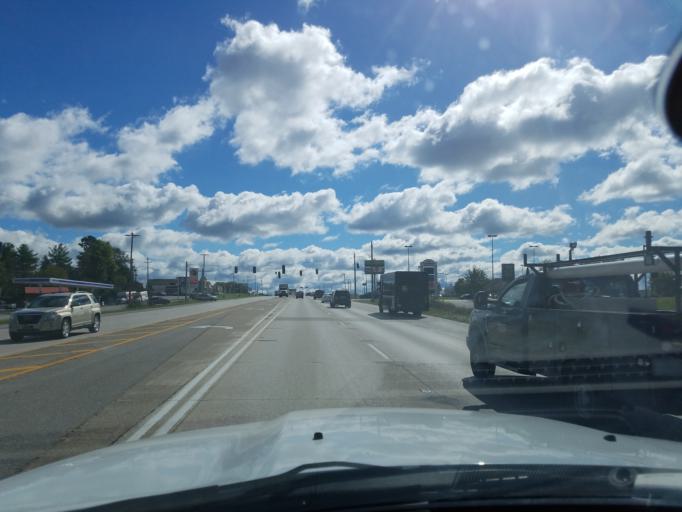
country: US
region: Kentucky
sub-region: Laurel County
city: London
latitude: 37.1098
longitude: -84.0898
